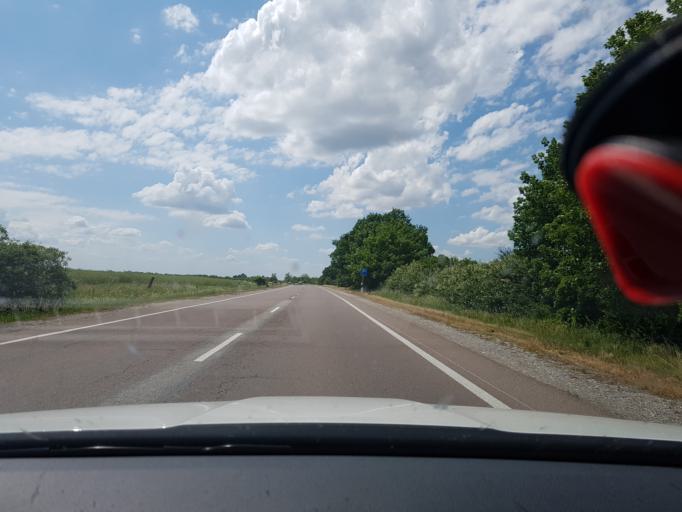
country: HU
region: Heves
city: Kompolt
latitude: 47.7626
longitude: 20.2059
